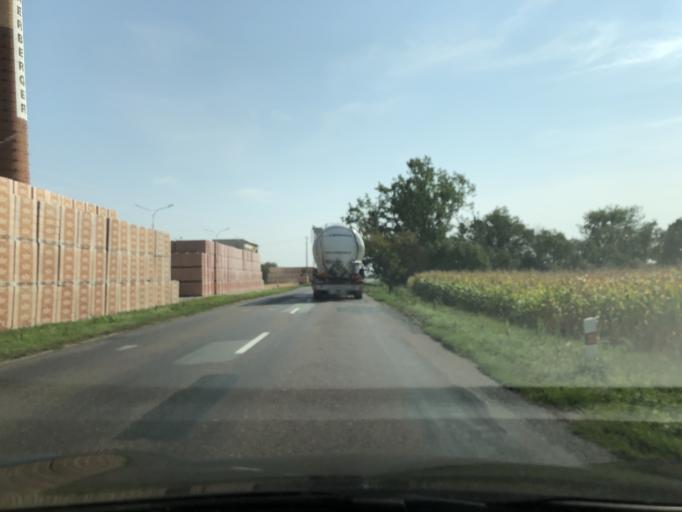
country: CZ
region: South Moravian
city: Novosedly
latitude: 48.8354
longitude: 16.5123
